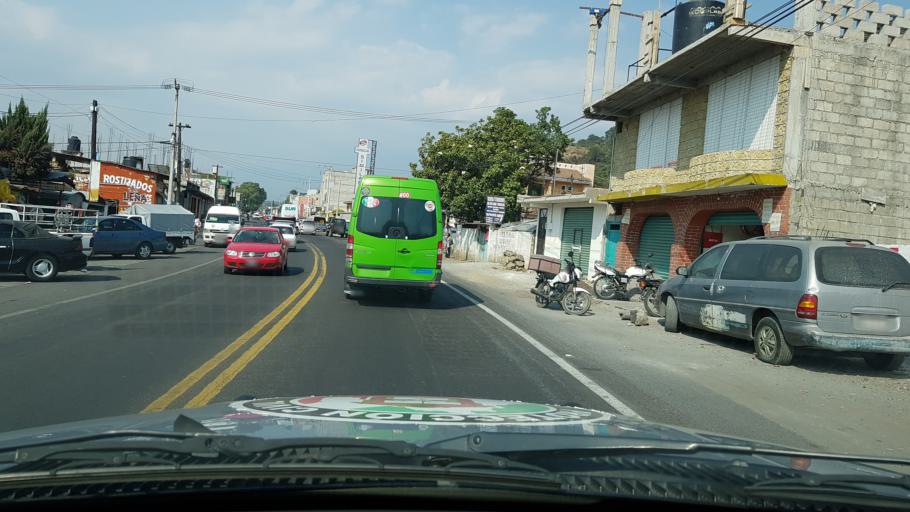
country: MX
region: Mexico
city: Tepetlixpa
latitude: 19.0256
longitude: -98.8180
